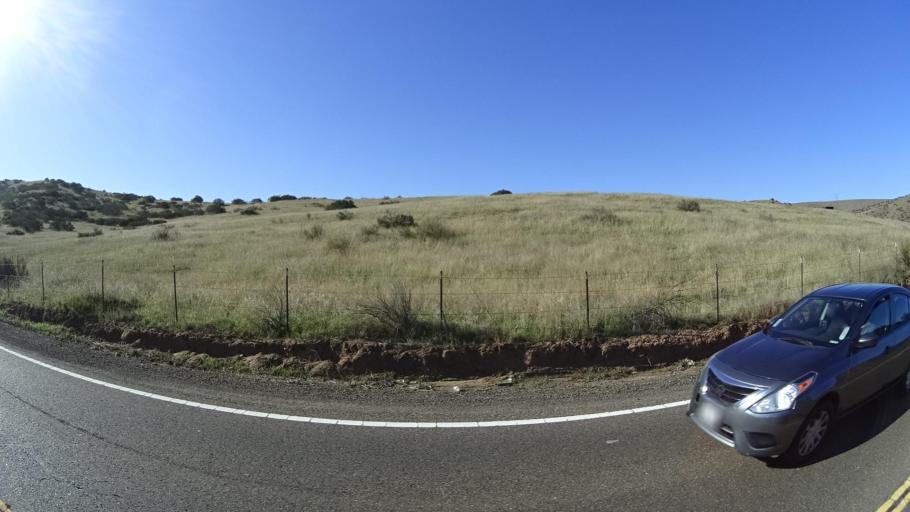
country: US
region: California
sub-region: San Diego County
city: Jamul
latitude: 32.6539
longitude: -116.8043
